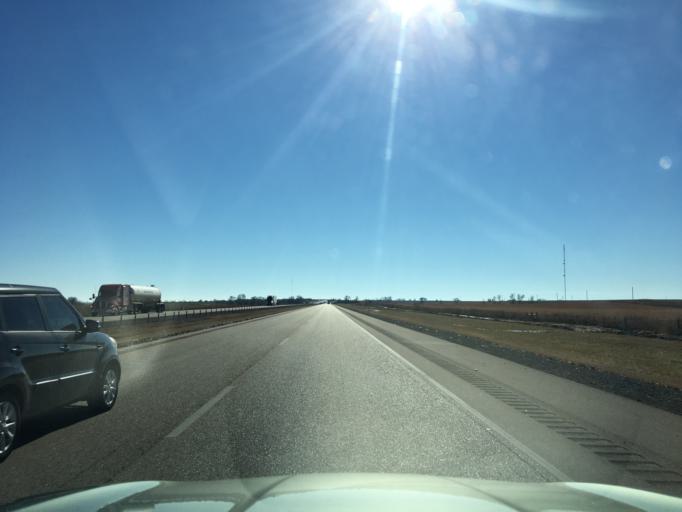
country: US
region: Oklahoma
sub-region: Kay County
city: Blackwell
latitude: 36.8920
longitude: -97.3536
